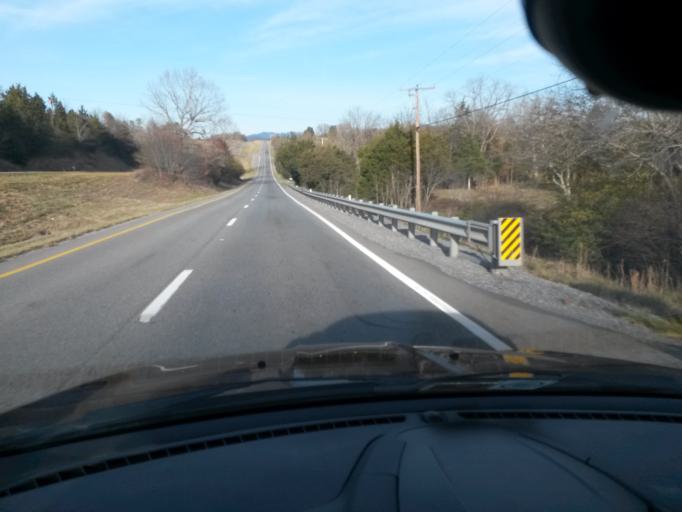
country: US
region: Virginia
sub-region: Botetourt County
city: Fincastle
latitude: 37.5323
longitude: -79.8696
